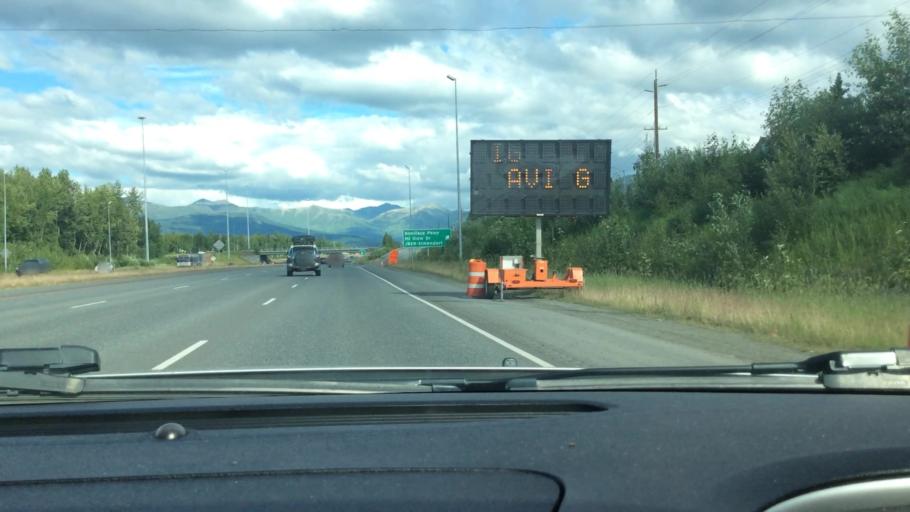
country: US
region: Alaska
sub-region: Anchorage Municipality
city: Anchorage
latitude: 61.2244
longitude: -149.7884
